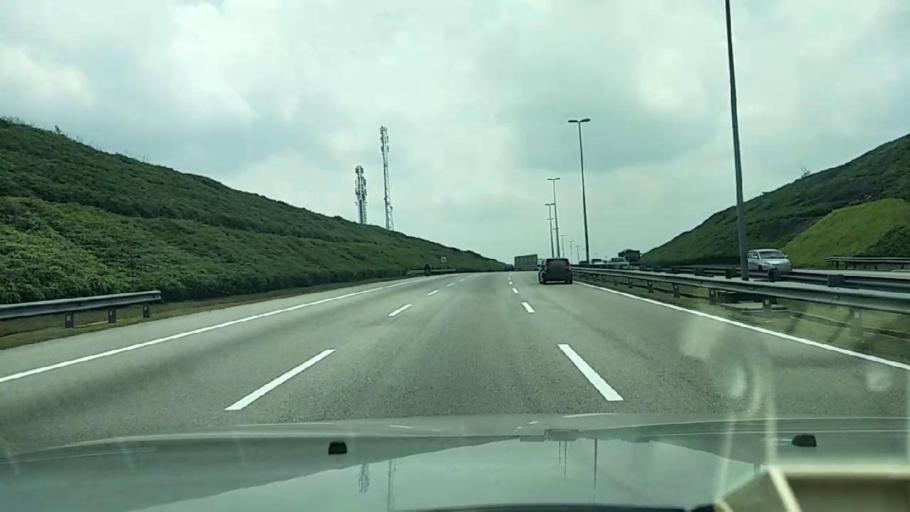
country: MY
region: Putrajaya
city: Putrajaya
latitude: 2.9621
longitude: 101.6550
